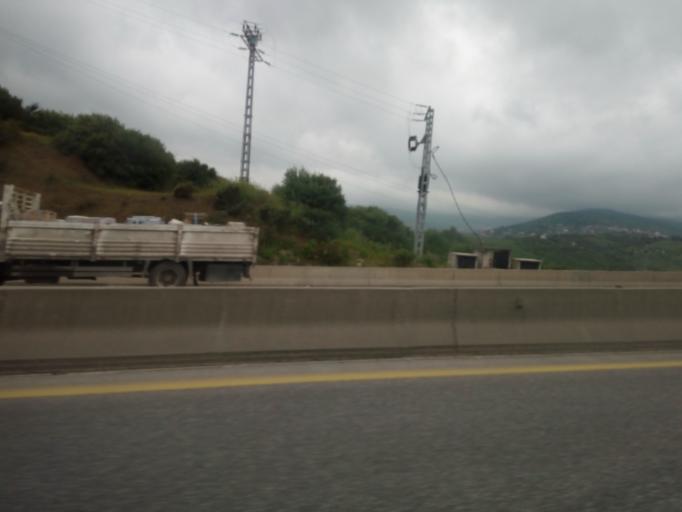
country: DZ
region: Bouira
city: Lakhdaria
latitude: 36.5839
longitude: 3.5394
